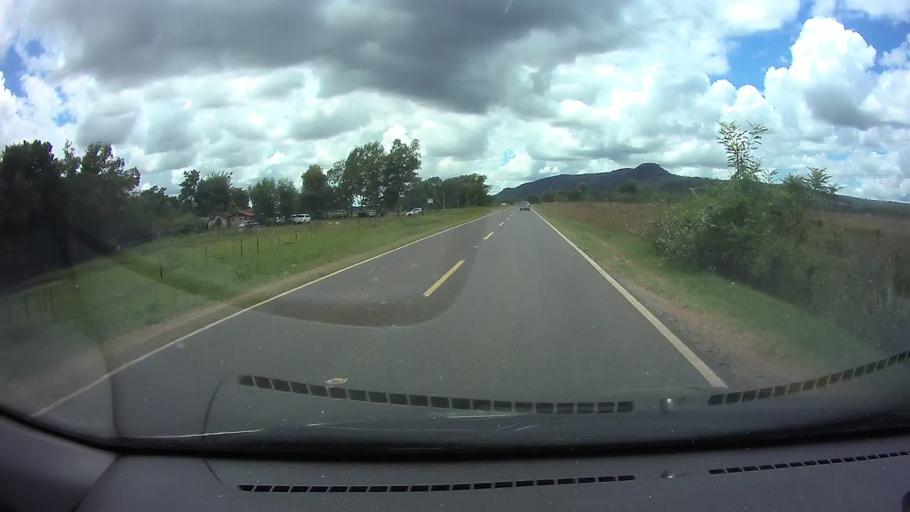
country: PY
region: Paraguari
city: Ybycui
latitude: -25.9100
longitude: -57.0022
